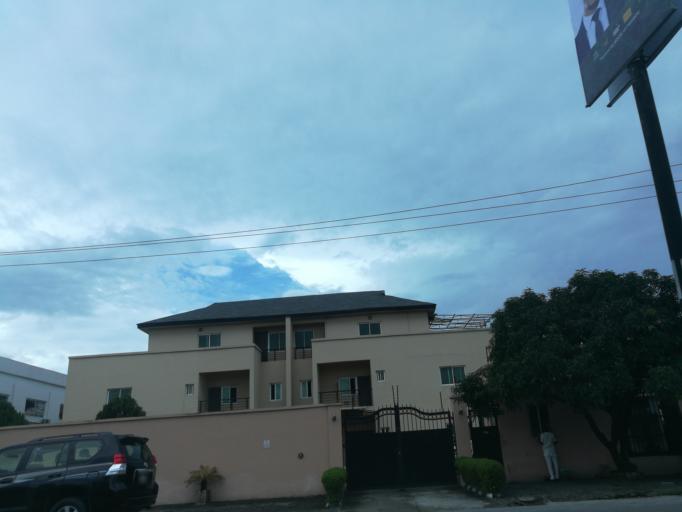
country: NG
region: Lagos
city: Ikoyi
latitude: 6.4478
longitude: 3.4754
